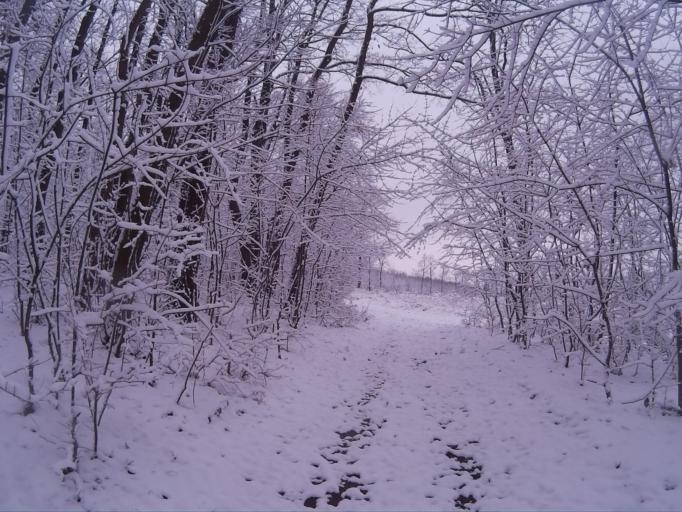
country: HU
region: Fejer
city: Szarliget
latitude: 47.5527
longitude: 18.5330
